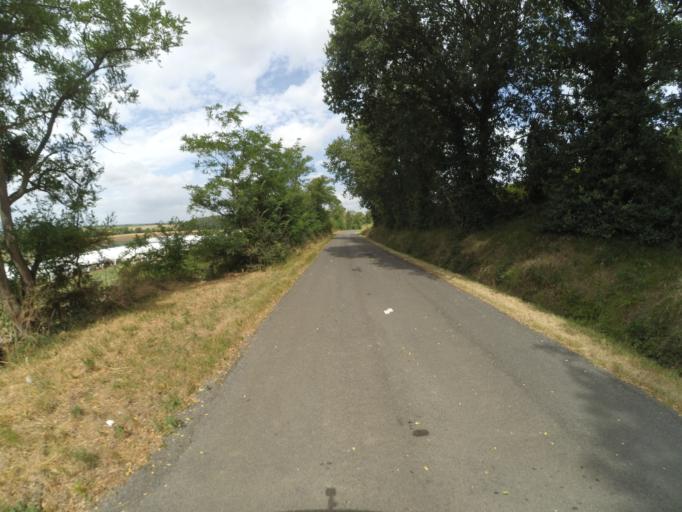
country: FR
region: Pays de la Loire
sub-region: Departement de Maine-et-Loire
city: Nueil-sur-Layon
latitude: 47.1782
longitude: -0.3466
